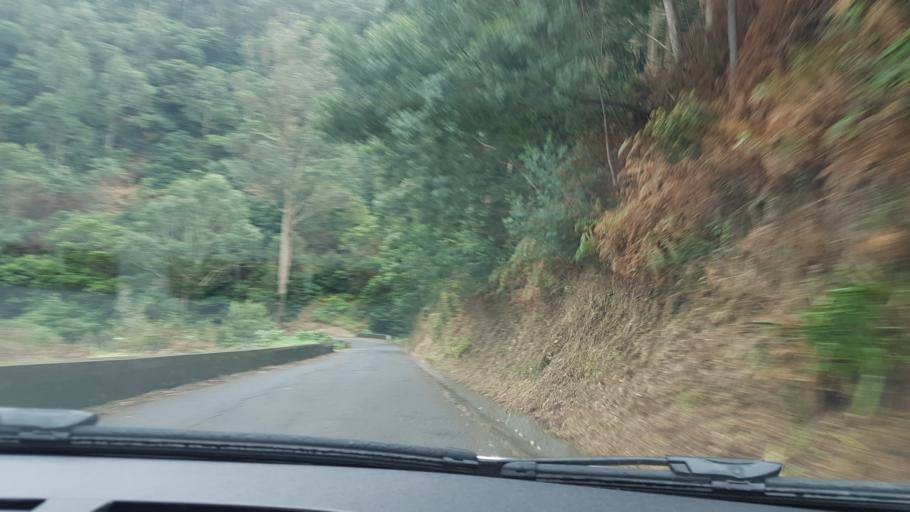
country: PT
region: Madeira
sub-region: Santa Cruz
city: Santa Cruz
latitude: 32.7282
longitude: -16.8100
